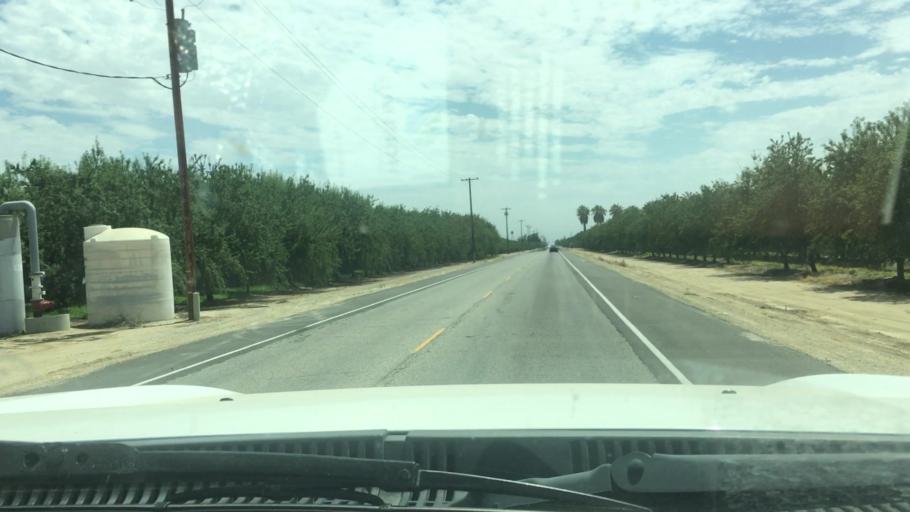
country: US
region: California
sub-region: Kern County
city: Wasco
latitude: 35.5580
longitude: -119.3453
